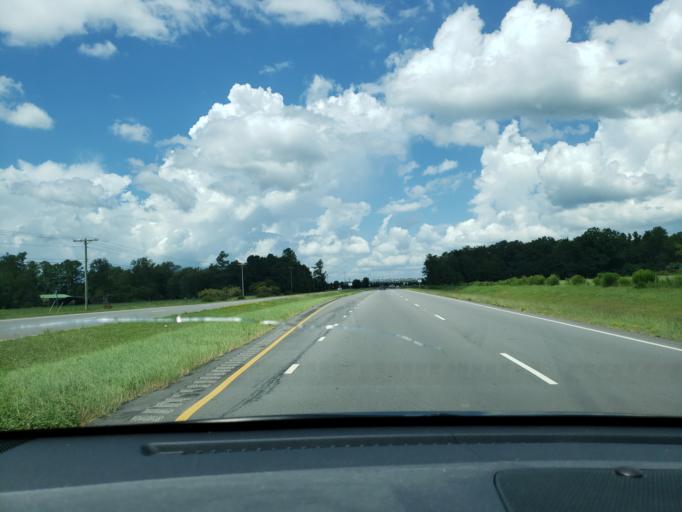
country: US
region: North Carolina
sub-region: Robeson County
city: Saint Pauls
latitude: 34.7386
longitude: -78.7991
